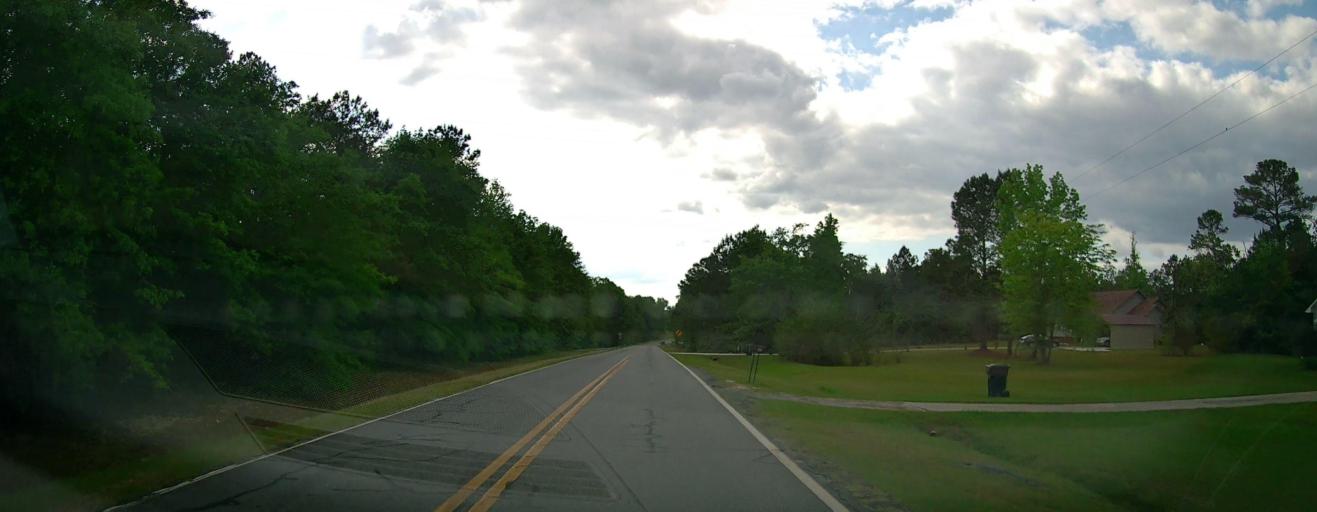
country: US
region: Georgia
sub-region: Baldwin County
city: Hardwick
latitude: 33.0605
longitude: -83.1321
